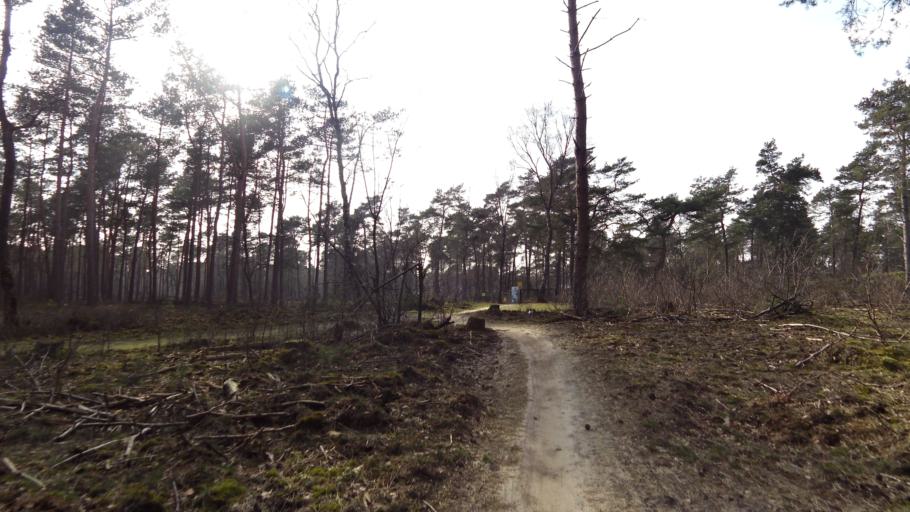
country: NL
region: Gelderland
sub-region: Gemeente Ede
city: Wekerom
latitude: 52.0861
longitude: 5.7383
